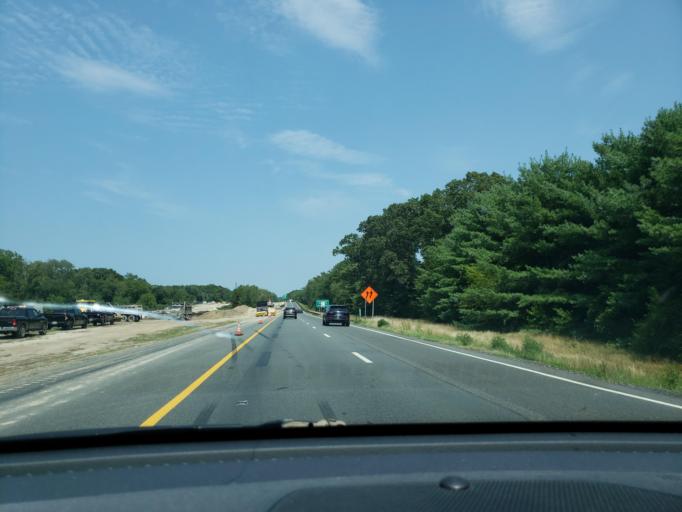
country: US
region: New Jersey
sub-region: Atlantic County
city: Northfield
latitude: 39.3761
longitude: -74.5814
